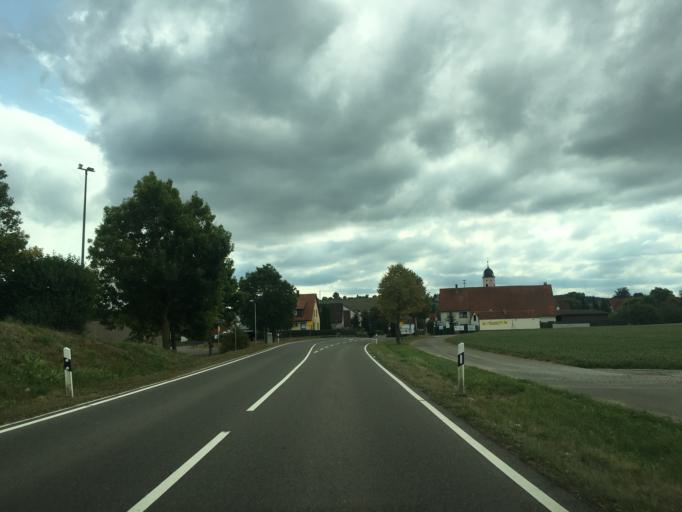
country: DE
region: Baden-Wuerttemberg
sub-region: Tuebingen Region
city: Sankt Johann
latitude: 48.3906
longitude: 9.2834
